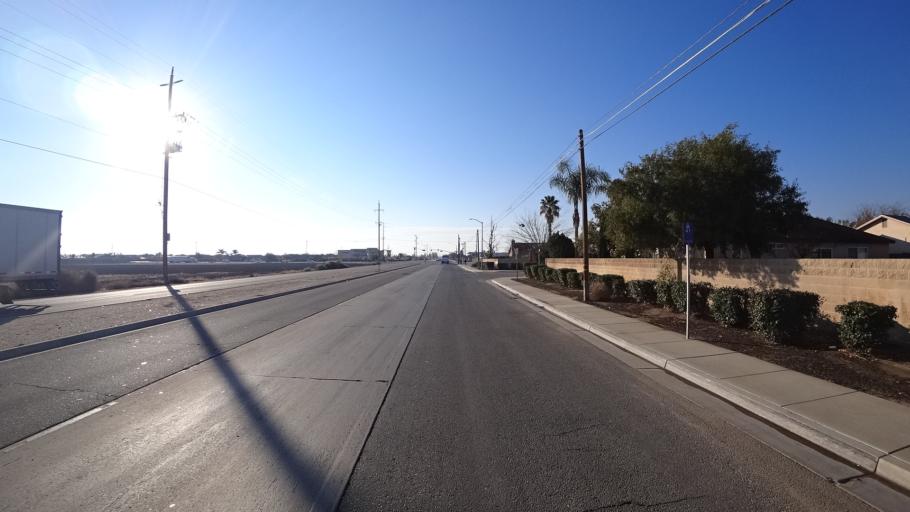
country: US
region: California
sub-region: Kern County
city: Greenfield
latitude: 35.2978
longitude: -119.0031
